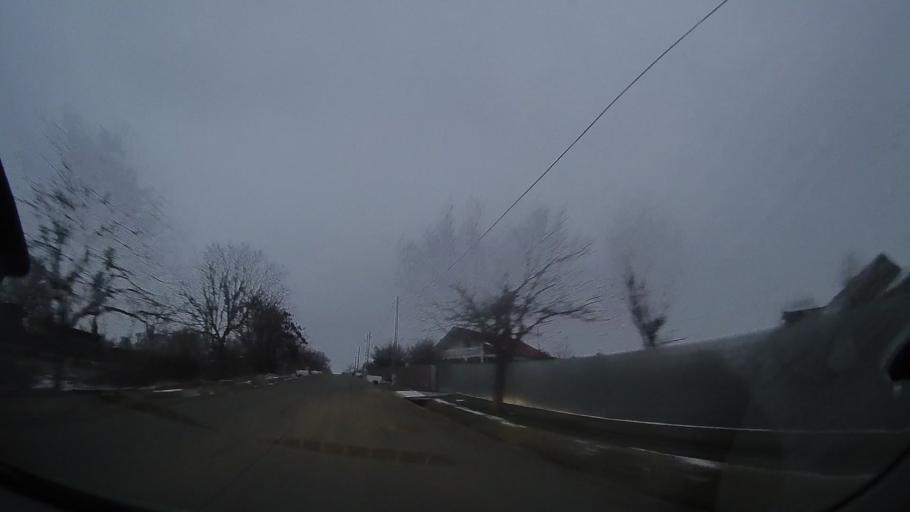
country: RO
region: Vaslui
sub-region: Comuna Gagesti
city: Gagesti
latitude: 46.3937
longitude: 27.9796
